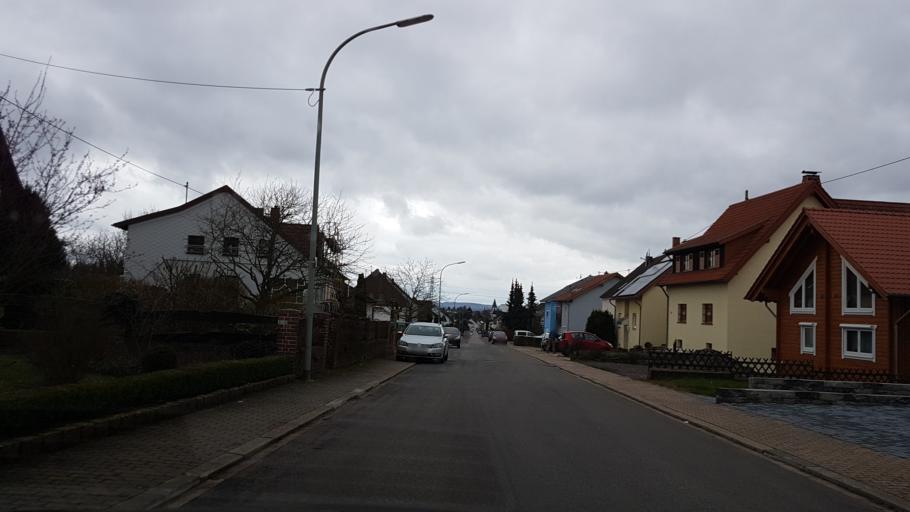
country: DE
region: Saarland
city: Schwalbach
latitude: 49.3079
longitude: 6.8336
